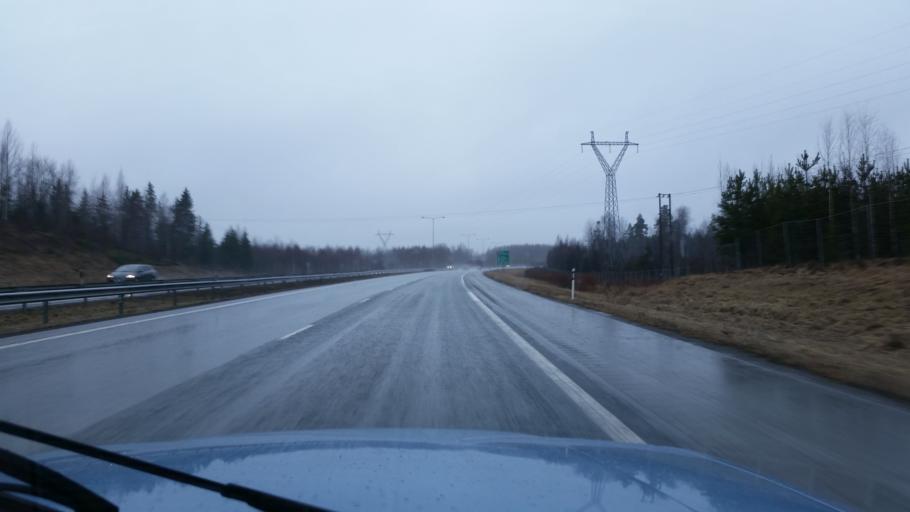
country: FI
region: Pirkanmaa
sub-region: Etelae-Pirkanmaa
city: Toijala
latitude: 61.1977
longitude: 23.8489
